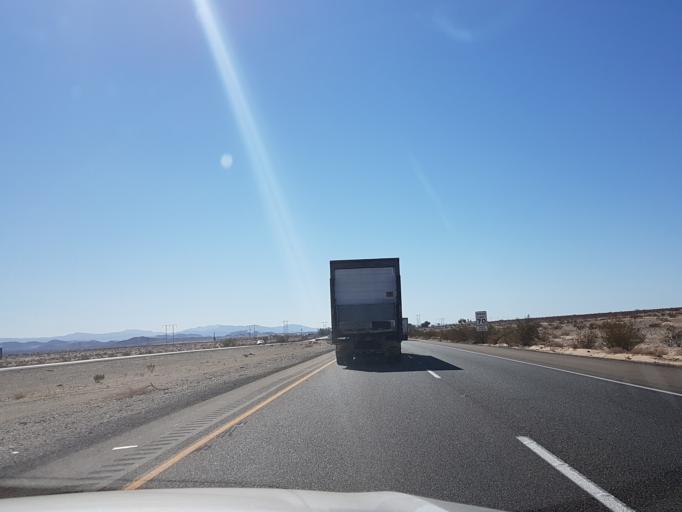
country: US
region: California
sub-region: San Bernardino County
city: Fort Irwin
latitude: 35.0398
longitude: -116.4603
